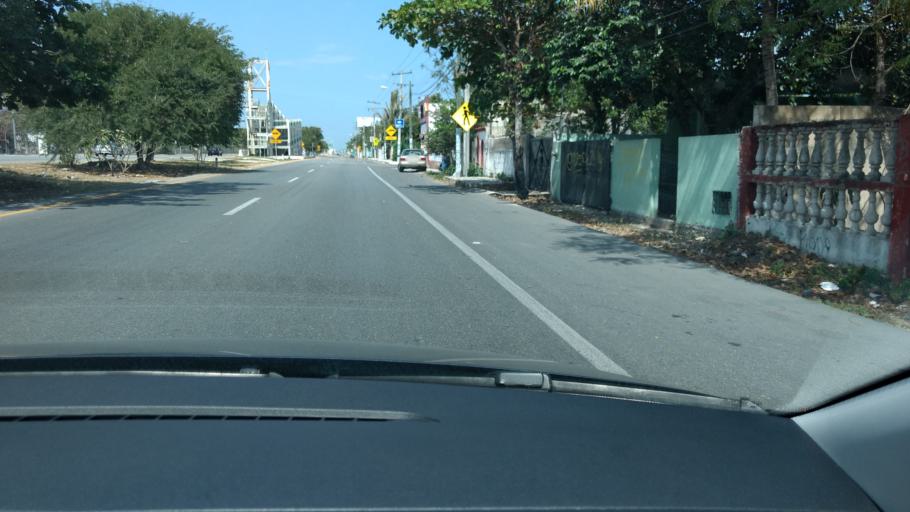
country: MX
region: Yucatan
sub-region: Kanasin
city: Kanasin
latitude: 20.9735
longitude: -89.5647
